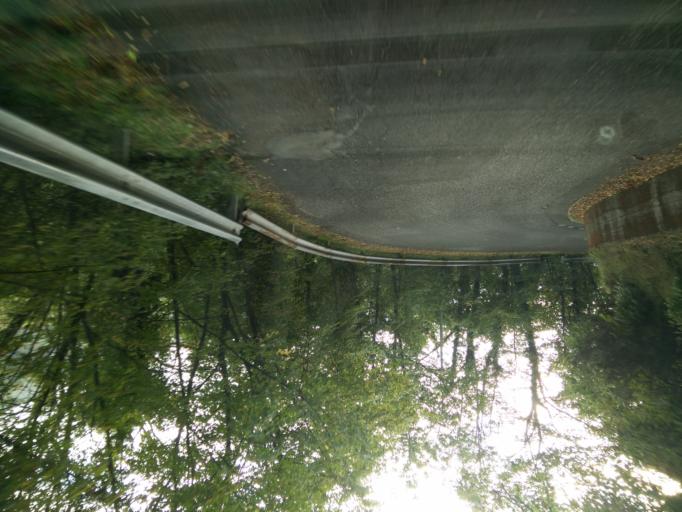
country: IT
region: Tuscany
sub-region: Provincia di Massa-Carrara
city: Pontremoli
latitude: 44.3714
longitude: 9.8393
